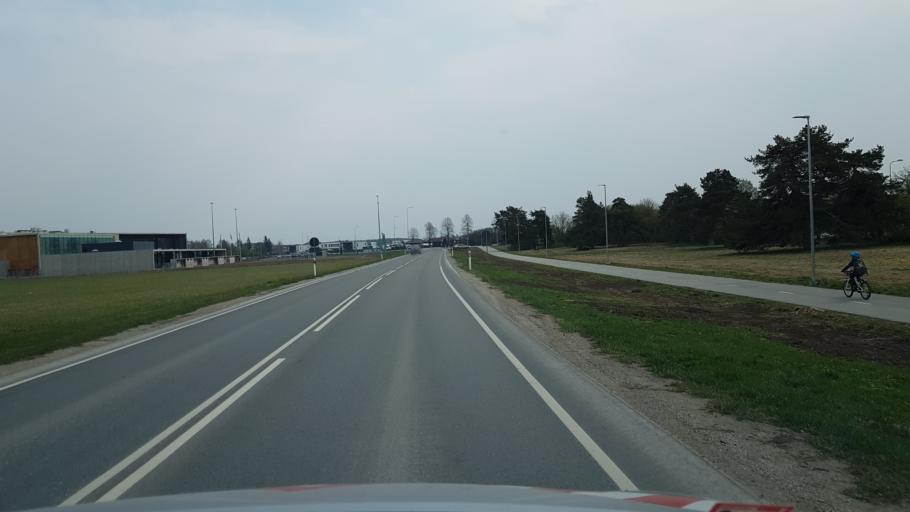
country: EE
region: Harju
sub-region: Kiili vald
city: Kiili
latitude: 59.3852
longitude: 24.8172
